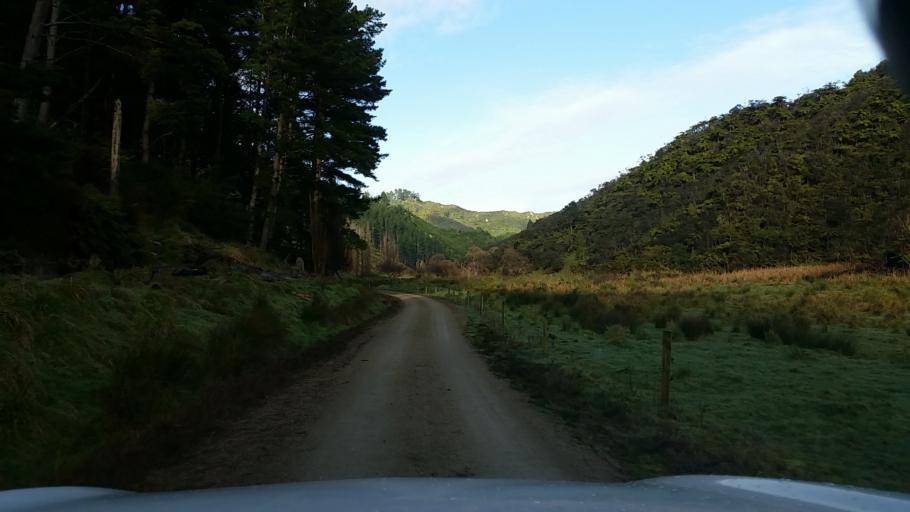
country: NZ
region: Taranaki
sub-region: South Taranaki District
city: Patea
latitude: -39.6833
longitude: 174.7644
